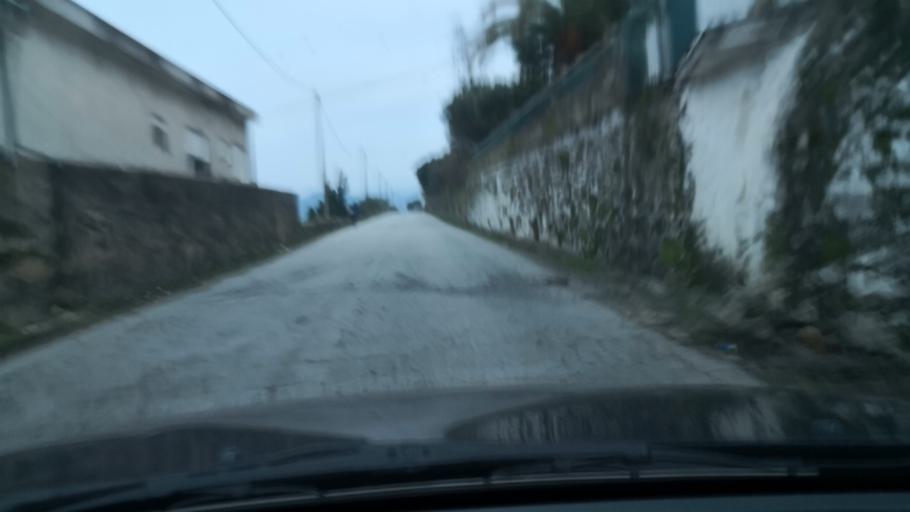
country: PT
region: Vila Real
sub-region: Peso da Regua
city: Peso da Regua
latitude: 41.1329
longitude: -7.7964
